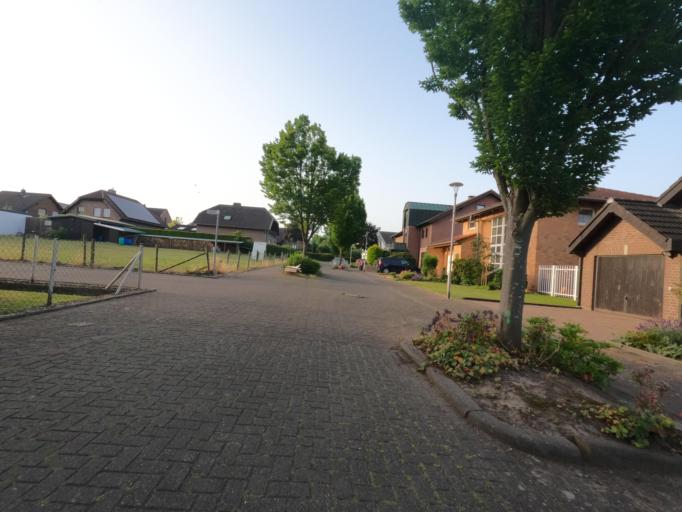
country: DE
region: North Rhine-Westphalia
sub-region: Regierungsbezirk Koln
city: Wassenberg
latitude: 51.0879
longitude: 6.1552
